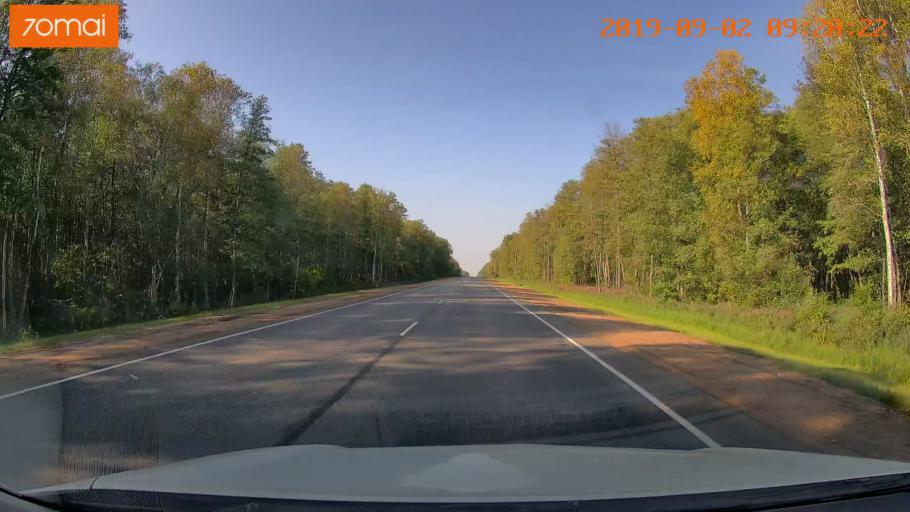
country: RU
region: Kaluga
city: Yukhnov
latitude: 54.8010
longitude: 35.3852
